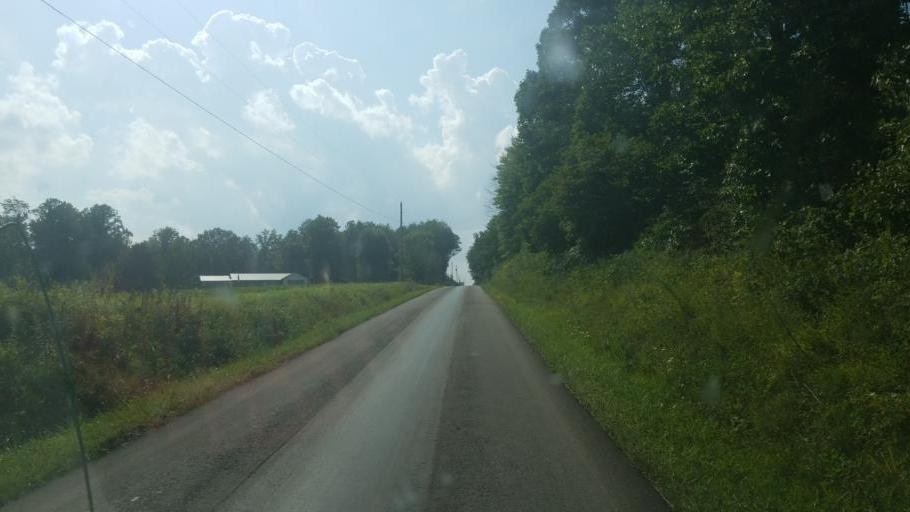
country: US
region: Ohio
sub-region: Wayne County
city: West Salem
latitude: 40.9525
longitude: -82.0392
